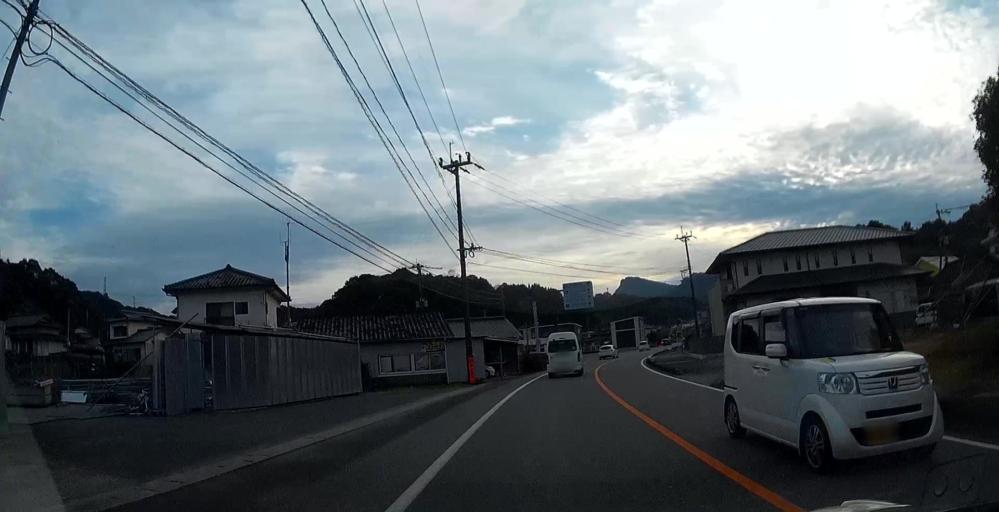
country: JP
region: Kumamoto
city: Yatsushiro
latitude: 32.5013
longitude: 130.4266
